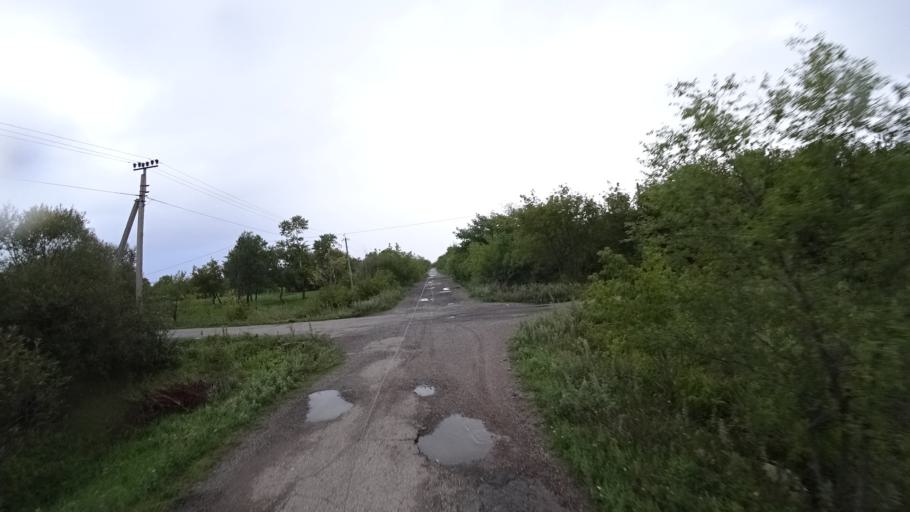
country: RU
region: Primorskiy
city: Chernigovka
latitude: 44.4022
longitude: 132.5316
